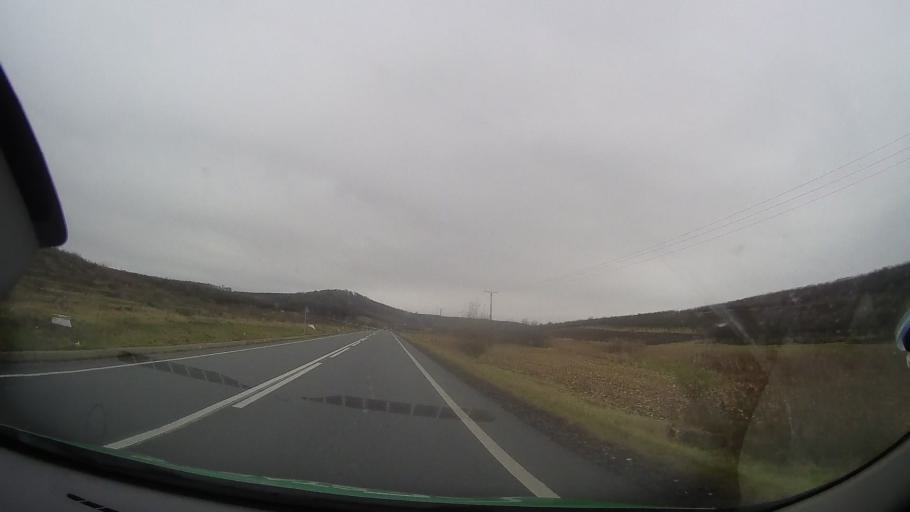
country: RO
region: Mures
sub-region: Comuna Breaza
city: Breaza
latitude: 46.7841
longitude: 24.6512
